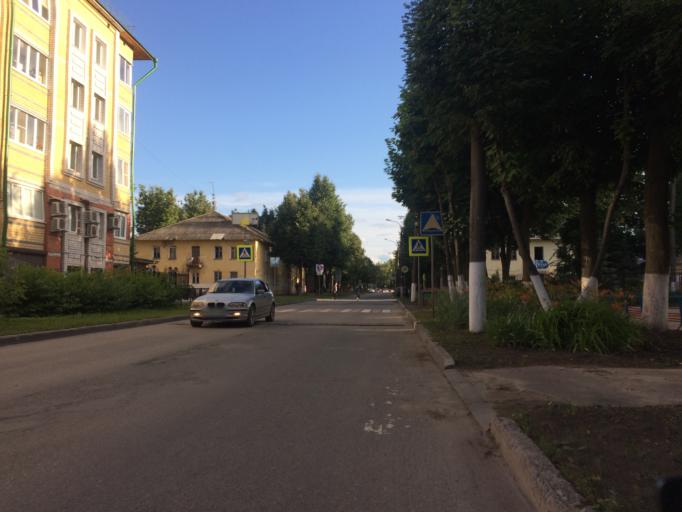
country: RU
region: Mariy-El
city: Yoshkar-Ola
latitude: 56.6357
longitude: 47.8806
